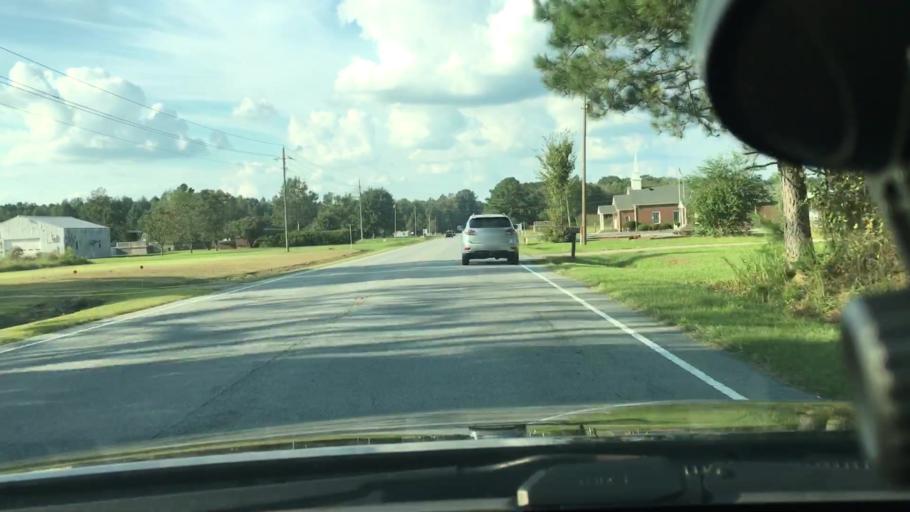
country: US
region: North Carolina
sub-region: Pitt County
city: Windsor
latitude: 35.4302
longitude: -77.2619
